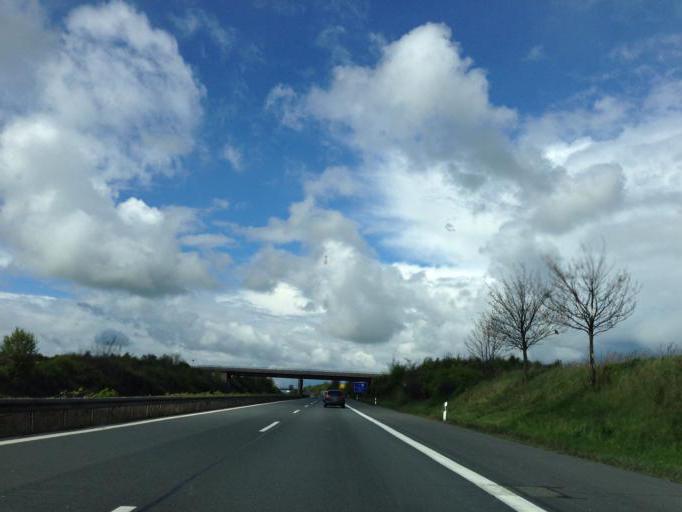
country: DE
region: Saxony-Anhalt
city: Oppin
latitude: 51.5485
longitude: 12.0097
